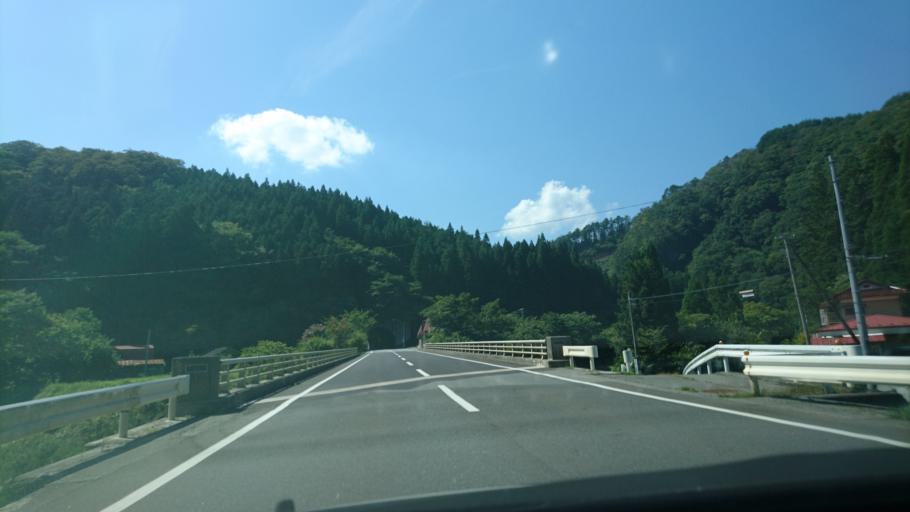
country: JP
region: Iwate
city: Ofunato
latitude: 39.0216
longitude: 141.5477
